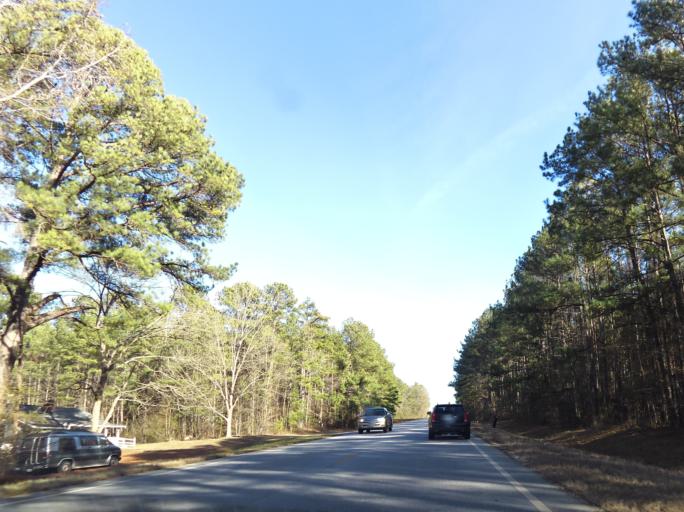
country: US
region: Georgia
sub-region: Crawford County
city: Roberta
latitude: 32.7226
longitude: -84.0292
